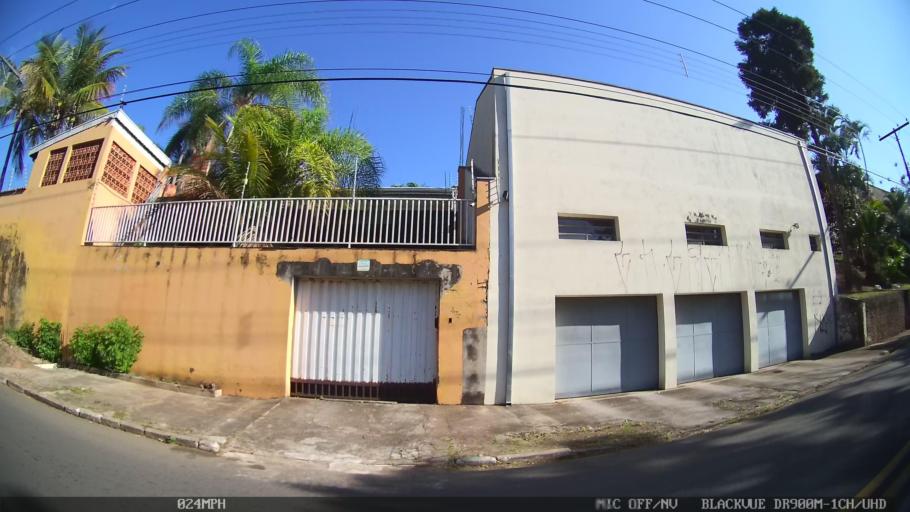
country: BR
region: Sao Paulo
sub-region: Campinas
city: Campinas
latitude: -22.9481
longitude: -47.0989
